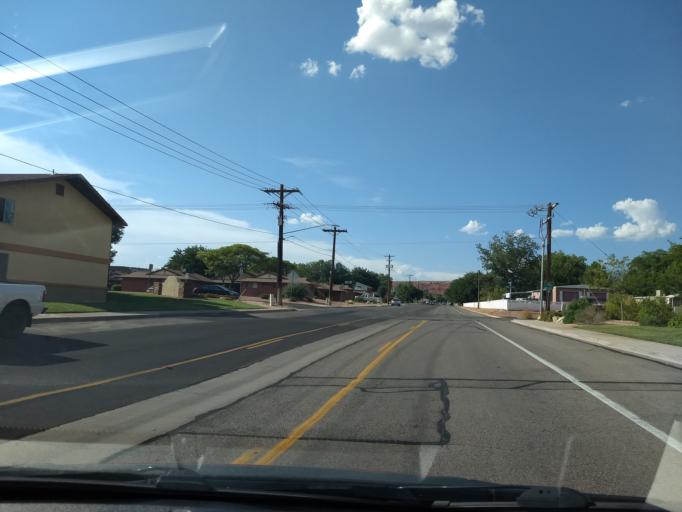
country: US
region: Utah
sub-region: Washington County
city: Saint George
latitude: 37.0918
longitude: -113.5749
